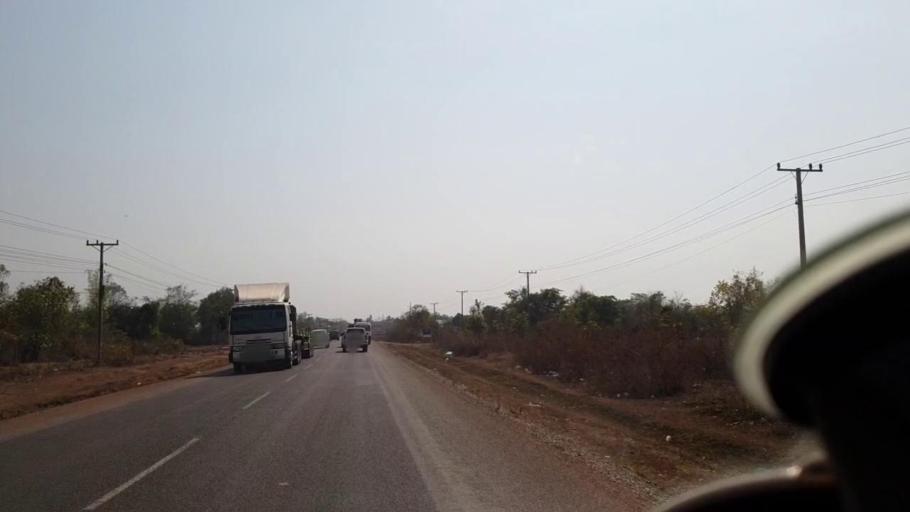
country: TH
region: Nong Khai
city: Nong Khai
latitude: 18.0585
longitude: 102.8126
